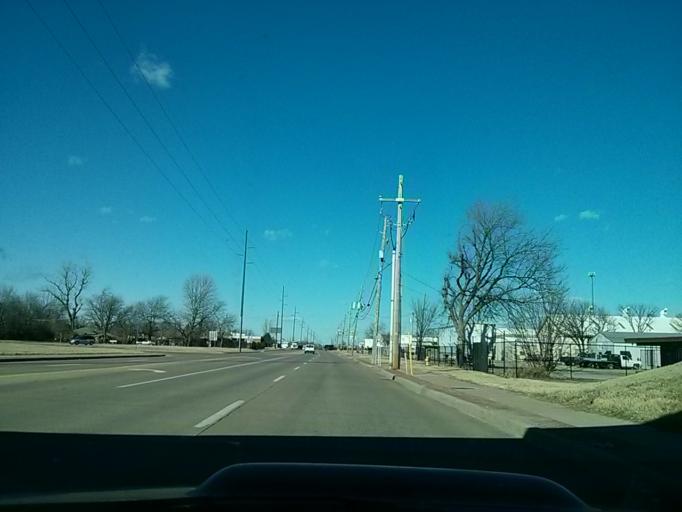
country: US
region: Oklahoma
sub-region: Tulsa County
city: Turley
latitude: 36.1988
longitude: -95.9581
